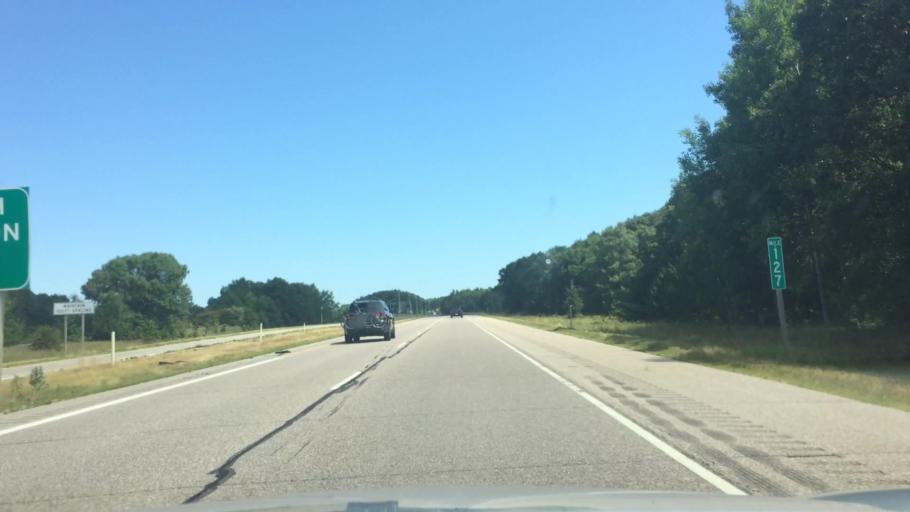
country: US
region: Wisconsin
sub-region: Marquette County
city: Westfield
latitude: 44.0733
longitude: -89.5365
